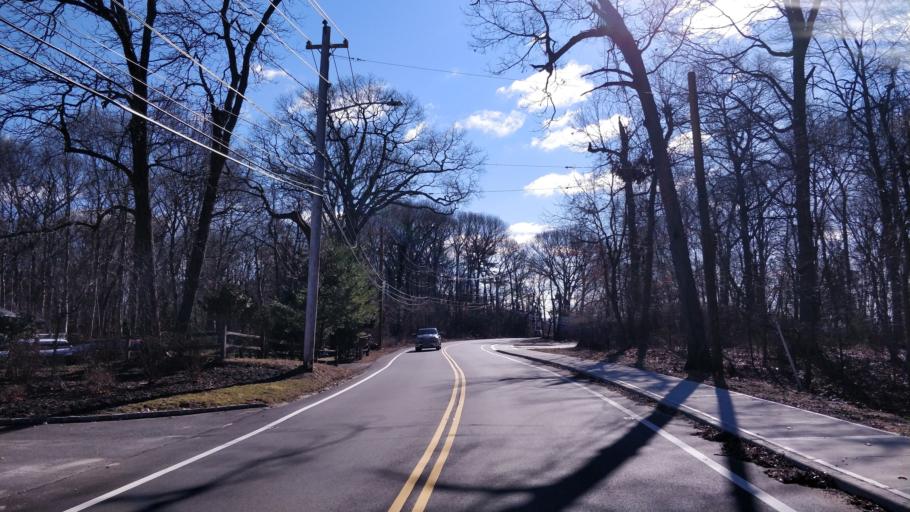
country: US
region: New York
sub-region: Suffolk County
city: Stony Brook
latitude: 40.9007
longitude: -73.1309
